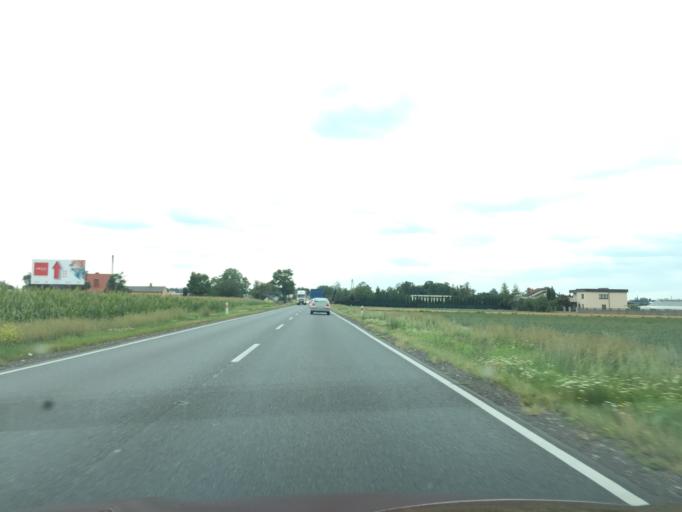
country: PL
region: Greater Poland Voivodeship
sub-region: Kalisz
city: Kalisz
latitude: 51.8296
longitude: 18.0947
